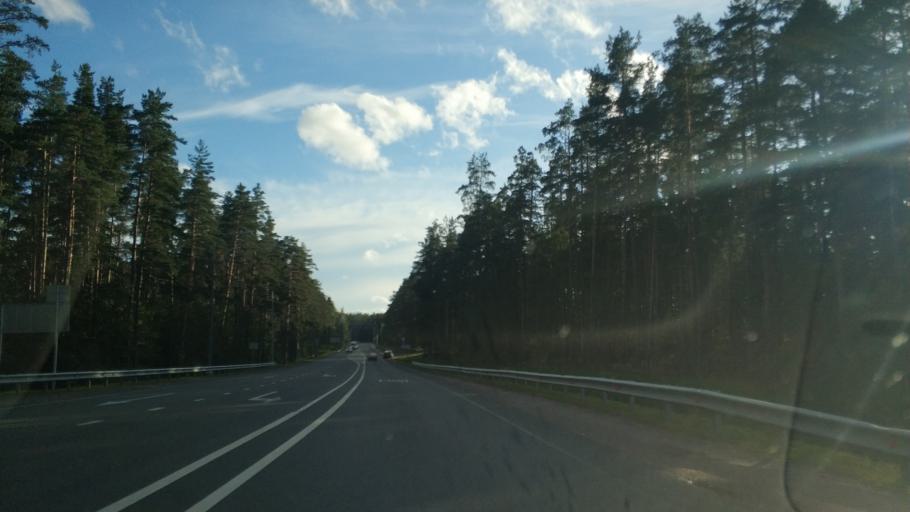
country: RU
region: Leningrad
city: Sapernoye
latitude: 60.7118
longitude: 29.9752
